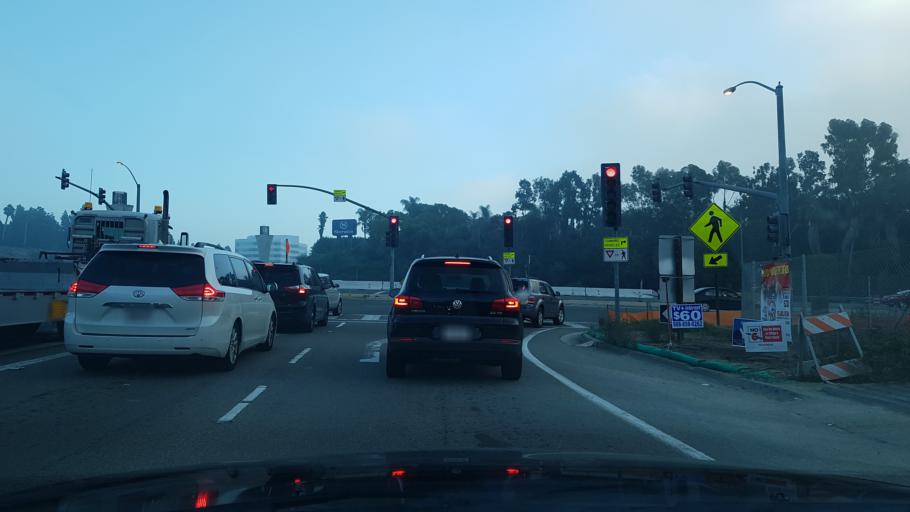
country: US
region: California
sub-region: San Diego County
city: La Jolla
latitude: 32.8722
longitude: -117.2308
